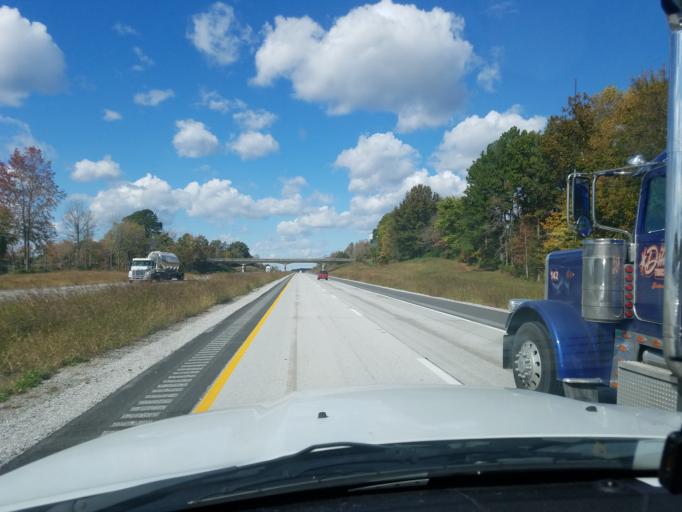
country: US
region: Kentucky
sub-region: Ohio County
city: Oak Grove
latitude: 37.3360
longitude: -86.7602
